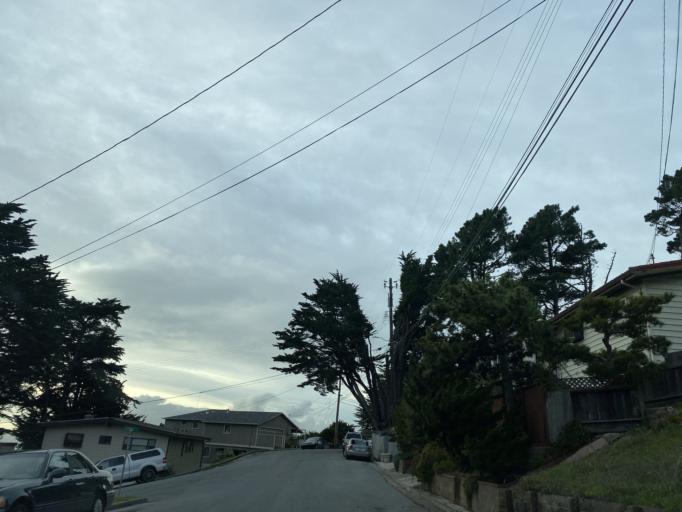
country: US
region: California
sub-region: San Mateo County
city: Broadmoor
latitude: 37.6547
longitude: -122.4855
